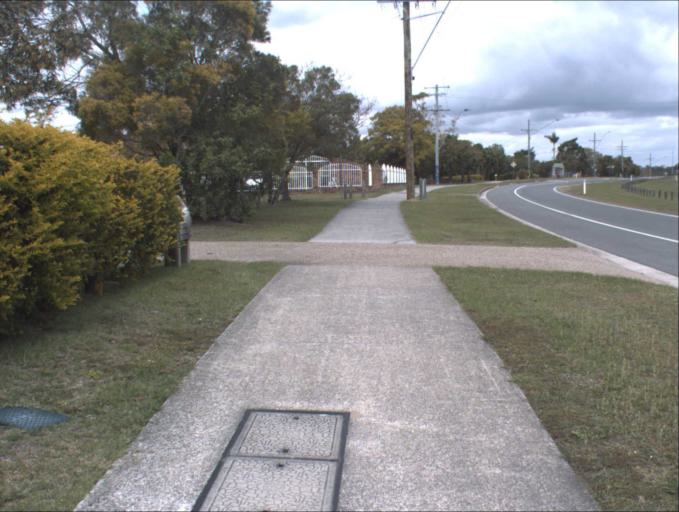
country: AU
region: Queensland
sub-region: Logan
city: Logan Reserve
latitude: -27.6805
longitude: 153.0610
